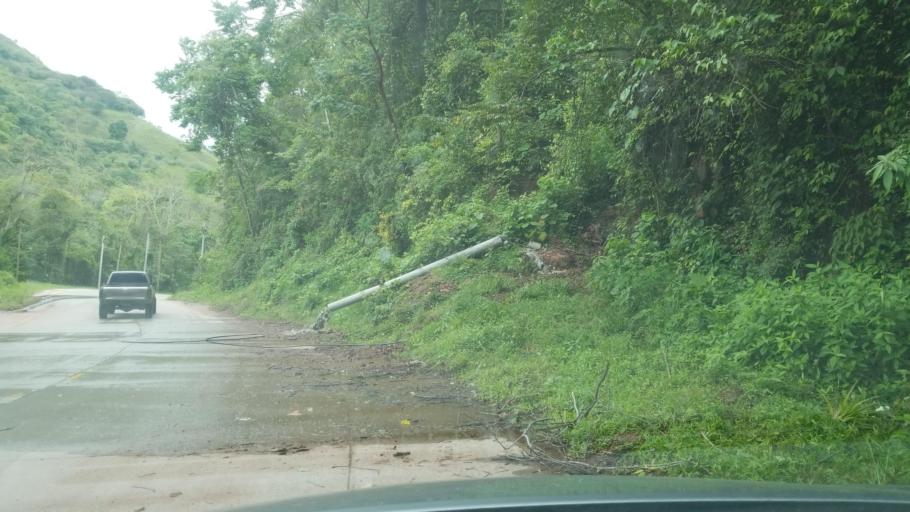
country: HN
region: Copan
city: San Jeronimo
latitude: 14.9311
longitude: -88.9576
